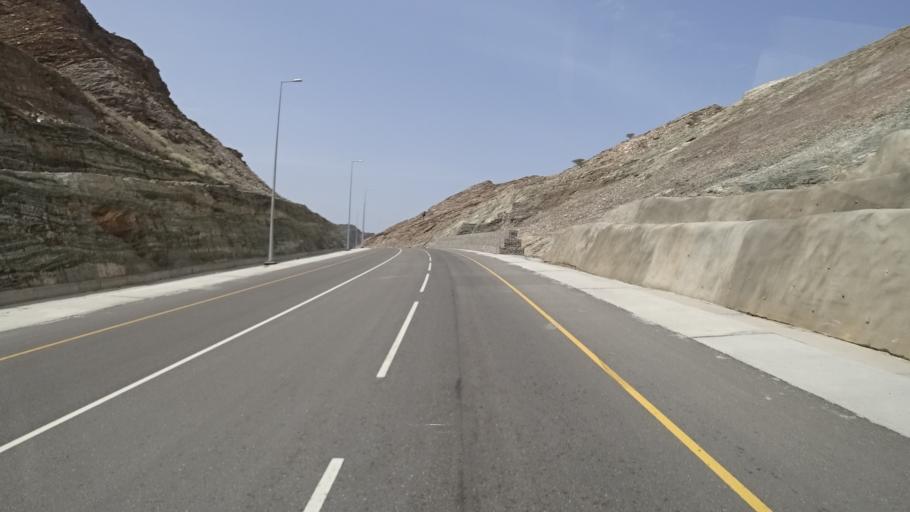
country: OM
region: Muhafazat Masqat
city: Muscat
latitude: 23.4439
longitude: 58.7581
